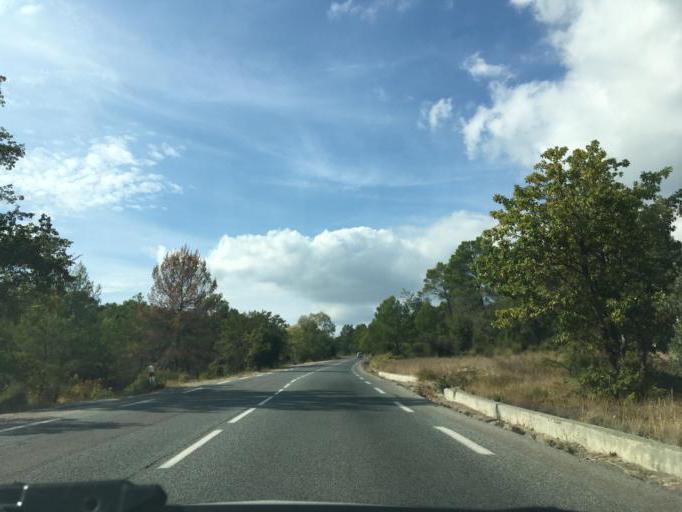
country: FR
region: Provence-Alpes-Cote d'Azur
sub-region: Departement du Var
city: Flayosc
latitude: 43.5439
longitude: 6.3463
